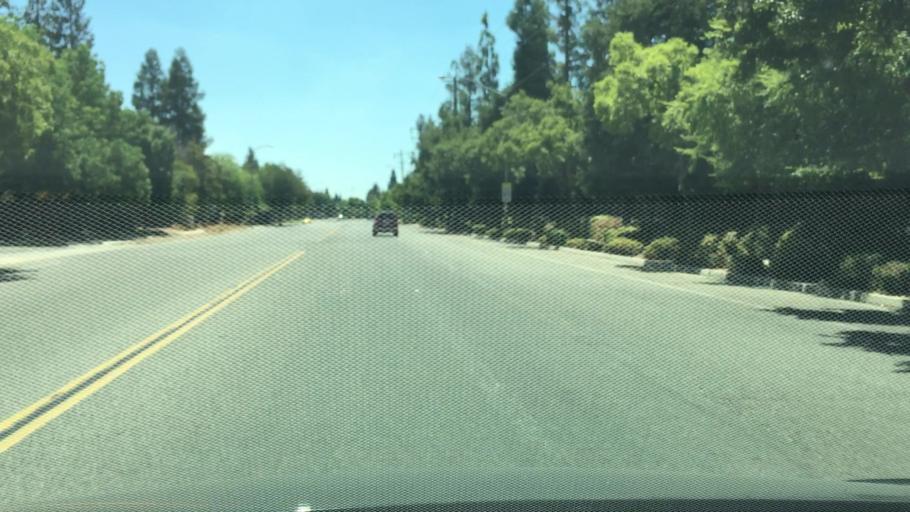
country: US
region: California
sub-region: Fresno County
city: Clovis
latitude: 36.8480
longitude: -119.7477
